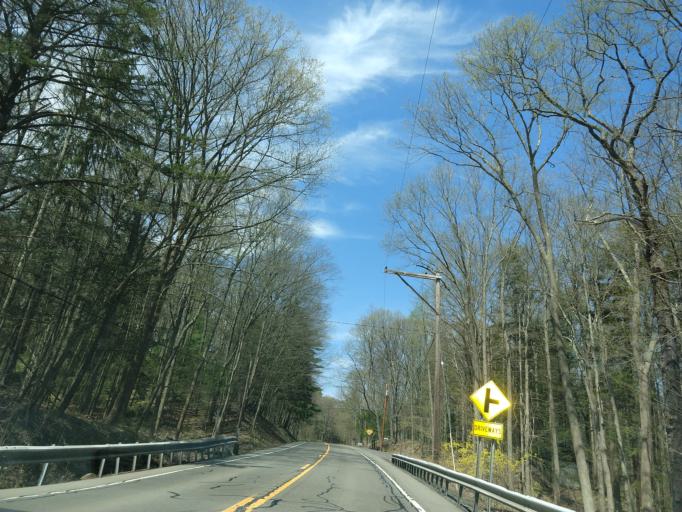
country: US
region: New York
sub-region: Tompkins County
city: Trumansburg
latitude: 42.5392
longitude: -76.5908
